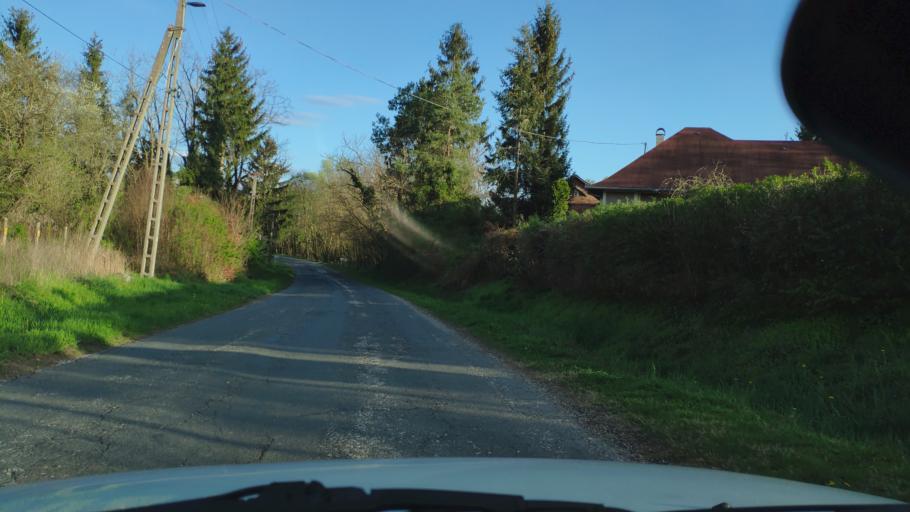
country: HU
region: Zala
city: Zalakomar
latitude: 46.4407
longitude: 17.1220
